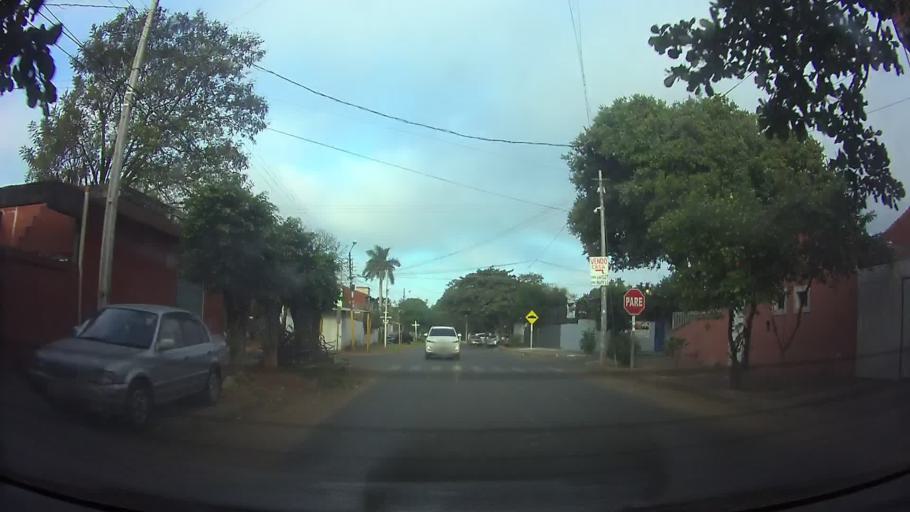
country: PY
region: Central
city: Fernando de la Mora
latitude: -25.3409
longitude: -57.5595
